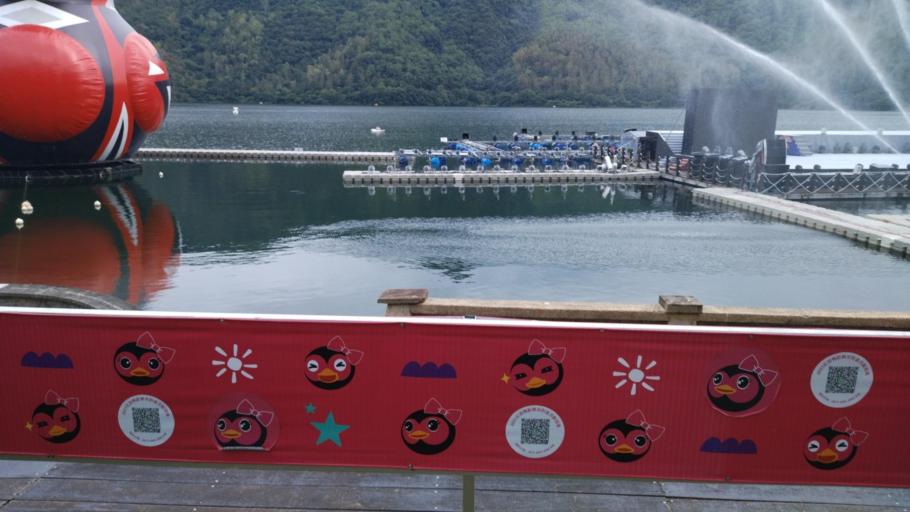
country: TW
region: Taiwan
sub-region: Hualien
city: Hualian
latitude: 23.9298
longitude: 121.5063
